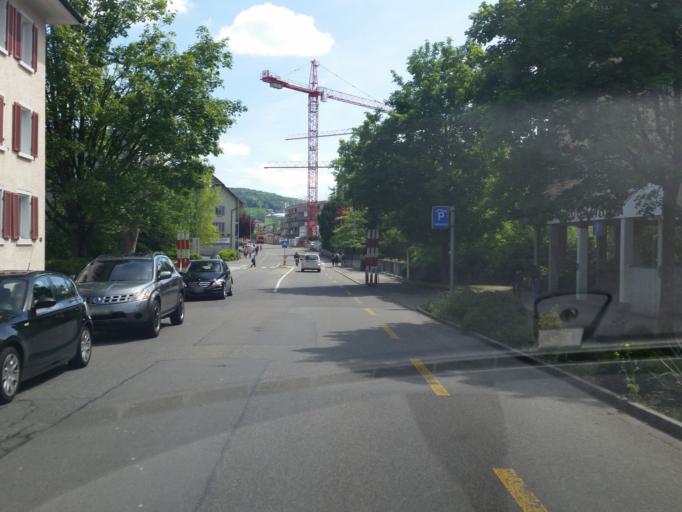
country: CH
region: Aargau
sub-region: Bezirk Bremgarten
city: Wohlen
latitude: 47.3483
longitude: 8.2771
